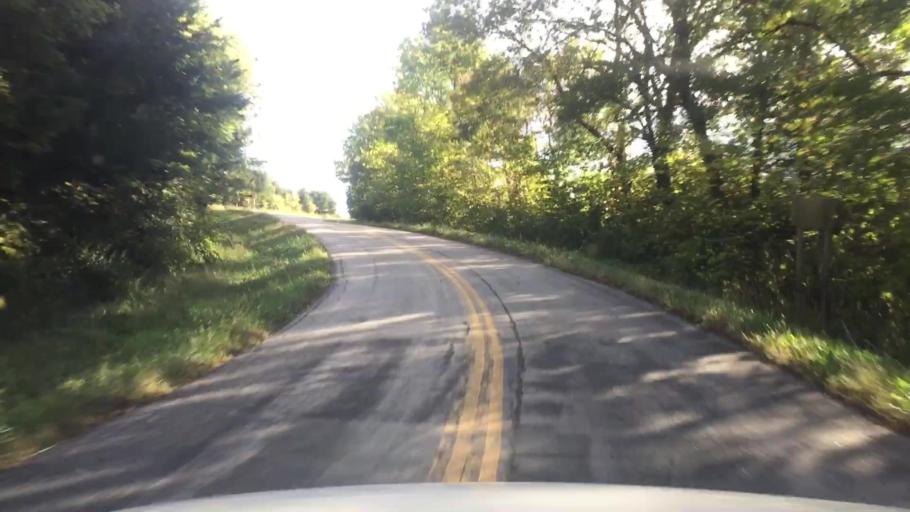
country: US
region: Missouri
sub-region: Howard County
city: New Franklin
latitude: 39.1049
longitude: -92.7703
